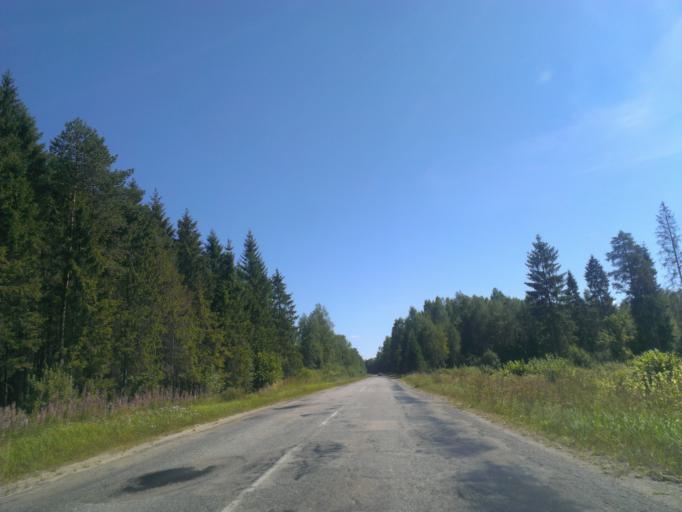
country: LV
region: Incukalns
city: Incukalns
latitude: 57.0269
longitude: 24.7461
